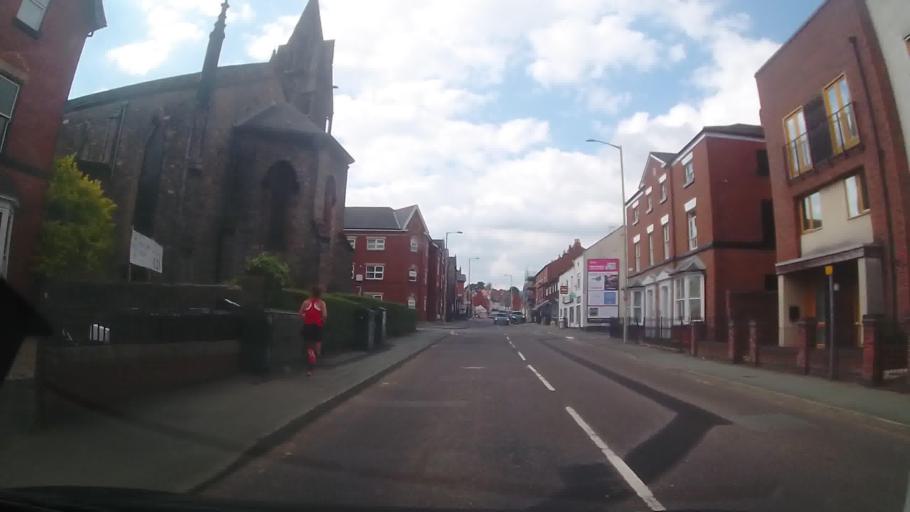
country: GB
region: England
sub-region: Shropshire
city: Oswestry
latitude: 52.8574
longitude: -3.0514
